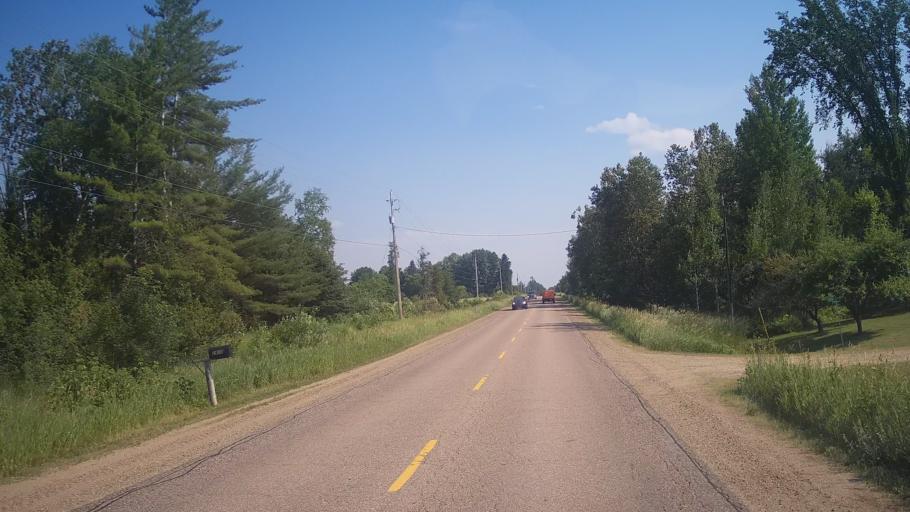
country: CA
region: Ontario
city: Pembroke
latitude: 45.5950
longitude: -77.2302
